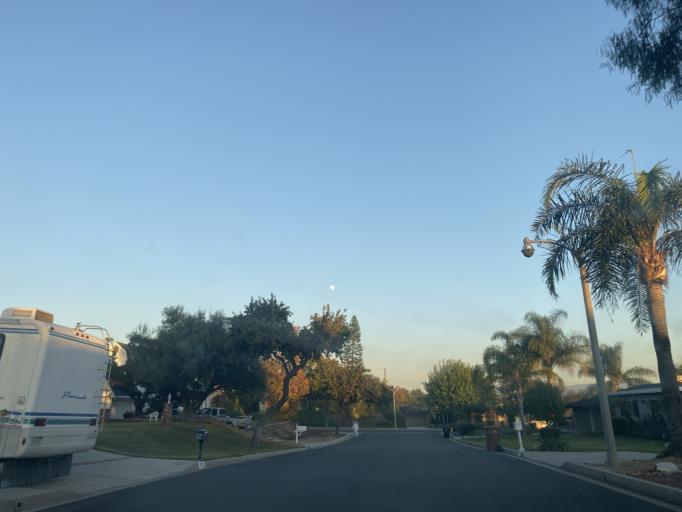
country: US
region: California
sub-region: Orange County
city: Fullerton
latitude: 33.8821
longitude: -117.9092
